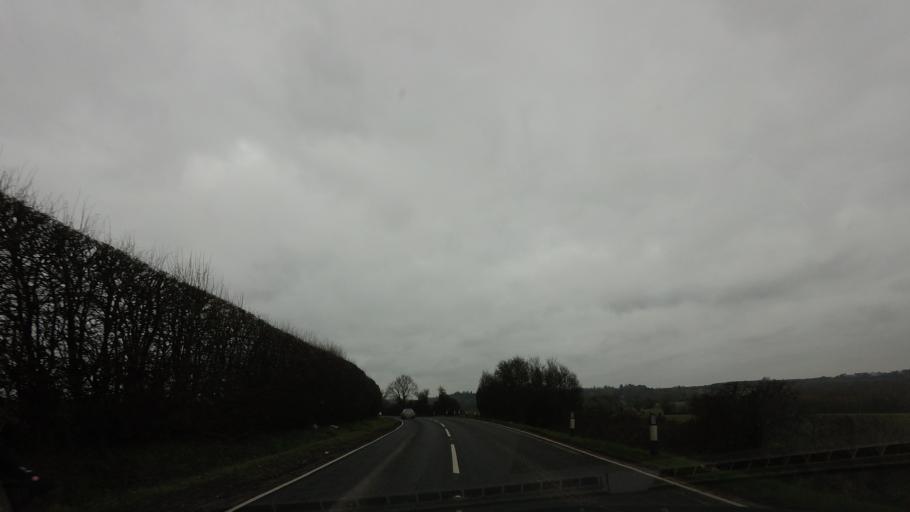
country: GB
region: England
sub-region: Kent
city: Marden
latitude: 51.2083
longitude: 0.5174
